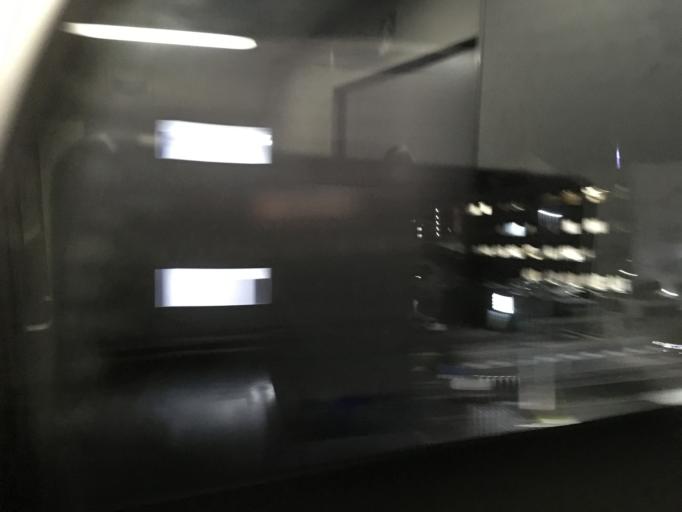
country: JP
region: Miyagi
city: Sendai
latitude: 38.2238
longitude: 140.8845
